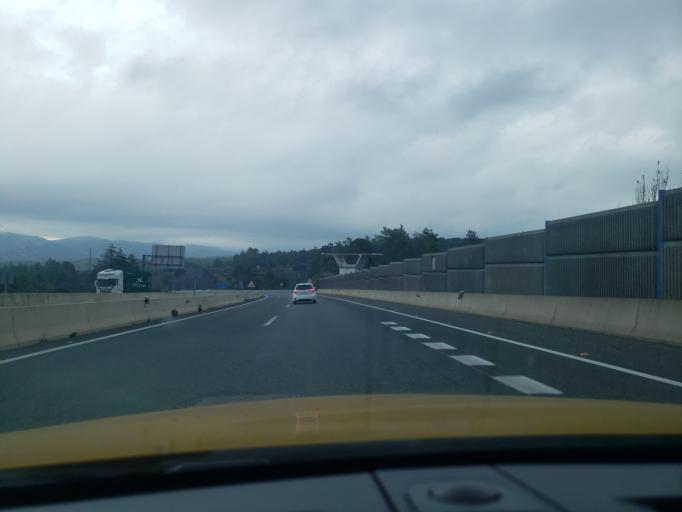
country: ES
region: Andalusia
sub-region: Provincia de Jaen
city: Santa Elena
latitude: 38.3454
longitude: -3.5377
